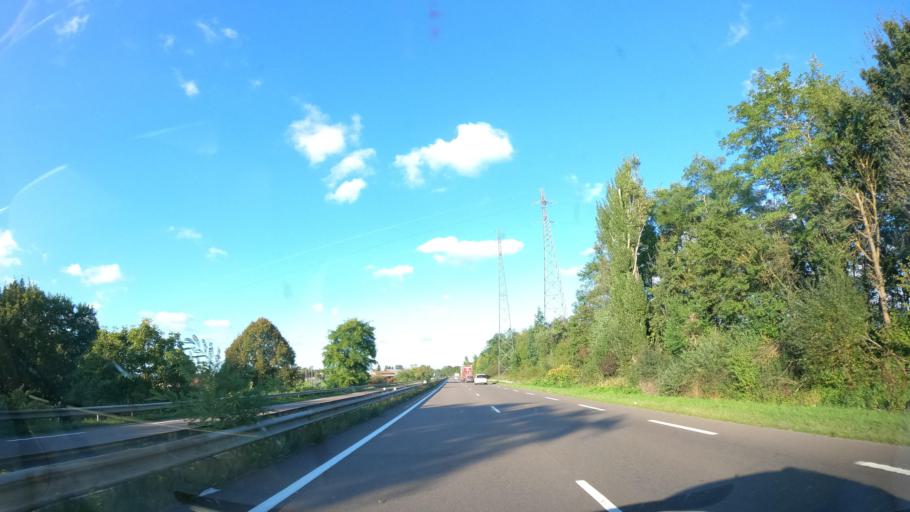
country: FR
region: Bourgogne
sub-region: Departement de Saone-et-Loire
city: Montceau-les-Mines
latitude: 46.6686
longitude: 4.3421
